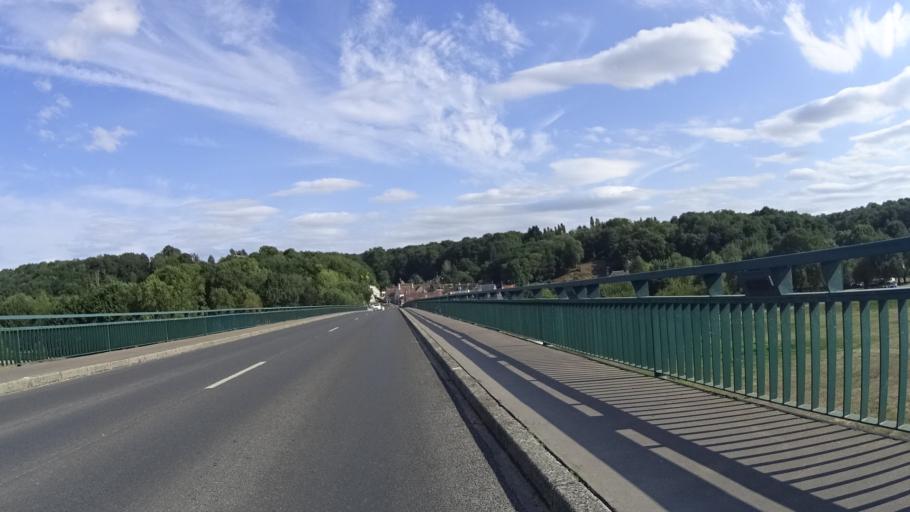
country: FR
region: Centre
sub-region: Departement du Loir-et-Cher
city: Chaumont-sur-Loire
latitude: 47.4845
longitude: 1.1913
